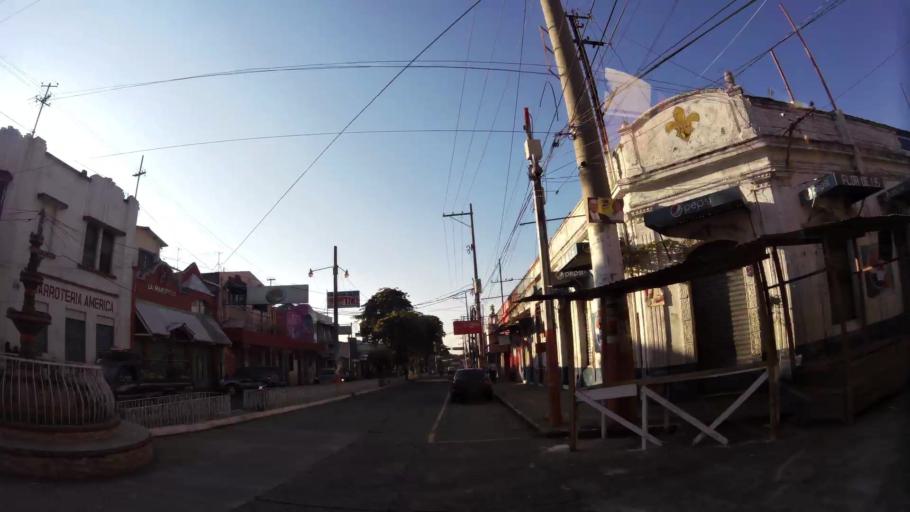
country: GT
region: Suchitepeque
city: Mazatenango
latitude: 14.5325
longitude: -91.5025
